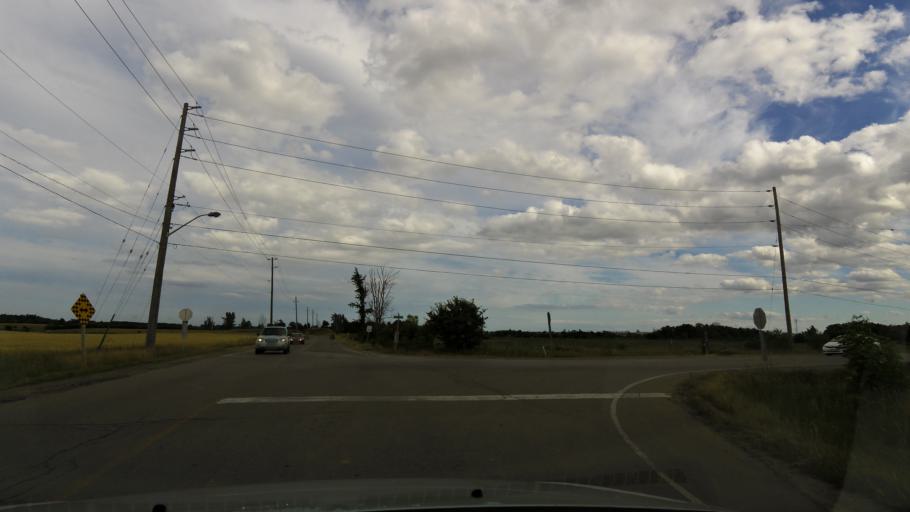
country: CA
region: Ontario
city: Brampton
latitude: 43.6673
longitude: -79.9025
